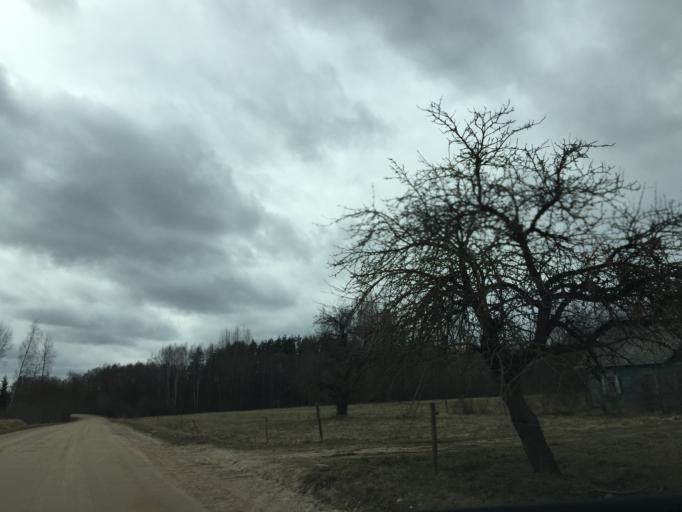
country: LV
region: Kraslavas Rajons
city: Kraslava
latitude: 55.9706
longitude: 27.0755
